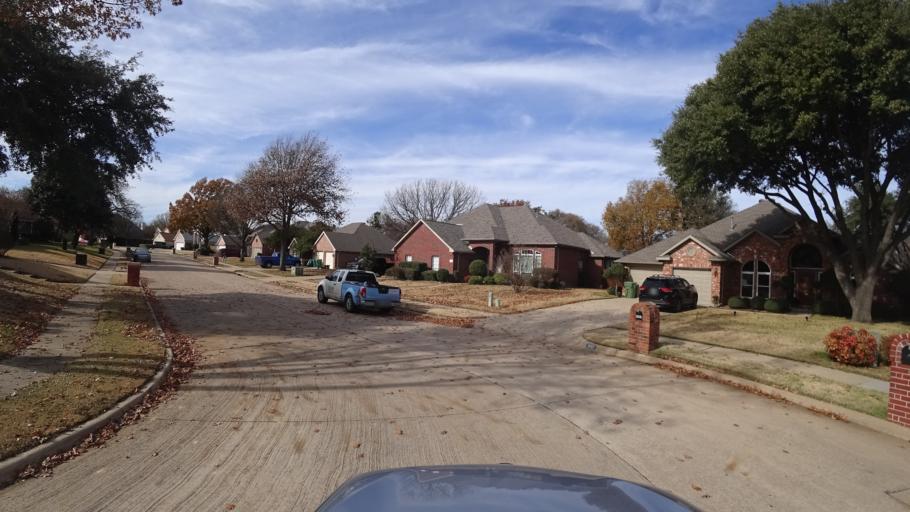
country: US
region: Texas
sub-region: Denton County
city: Highland Village
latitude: 33.0833
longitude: -97.0331
